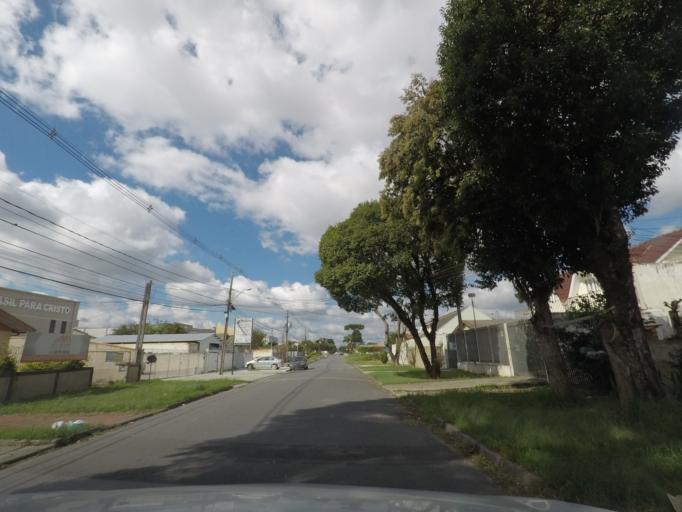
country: BR
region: Parana
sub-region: Sao Jose Dos Pinhais
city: Sao Jose dos Pinhais
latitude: -25.4970
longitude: -49.2301
